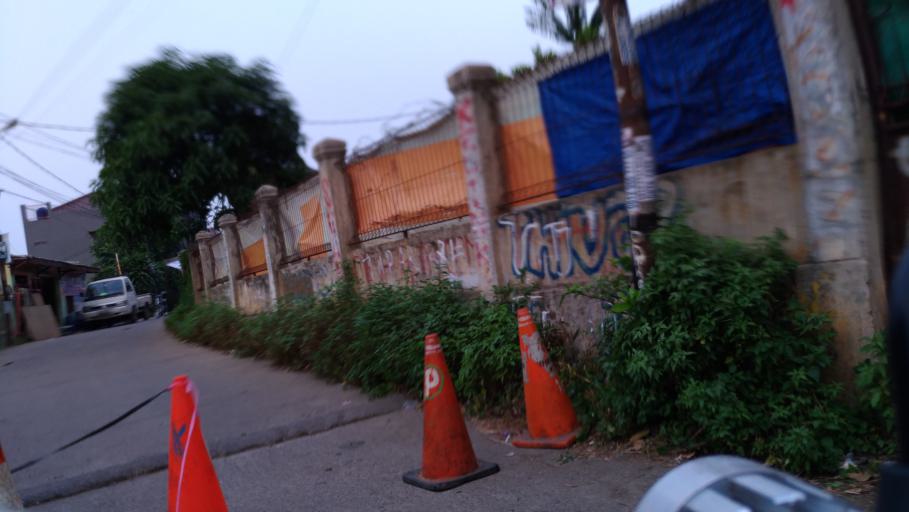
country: ID
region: West Java
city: Depok
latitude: -6.3590
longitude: 106.8672
